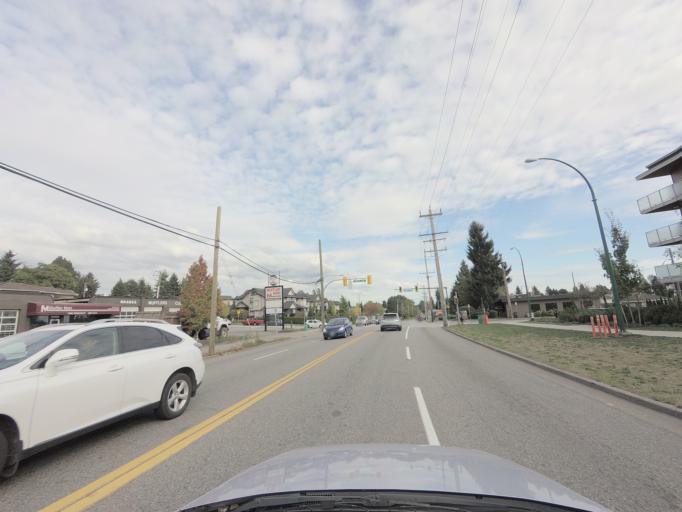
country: CA
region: British Columbia
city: New Westminster
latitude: 49.2158
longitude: -122.9415
